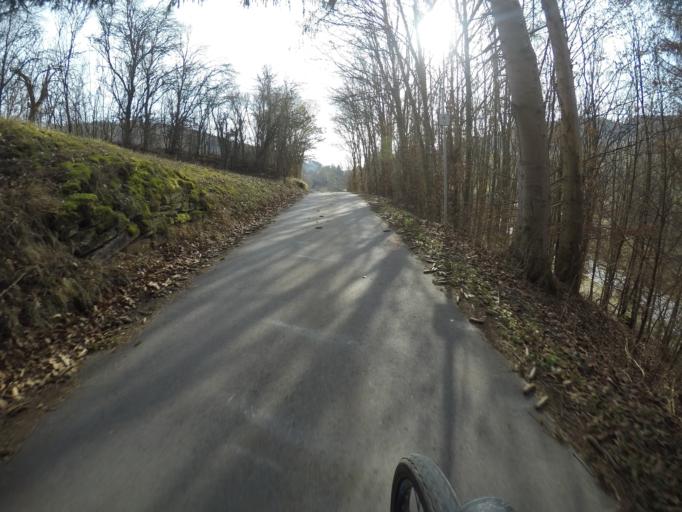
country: DE
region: Baden-Wuerttemberg
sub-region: Karlsruhe Region
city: Wildberg
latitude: 48.6304
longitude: 8.7709
